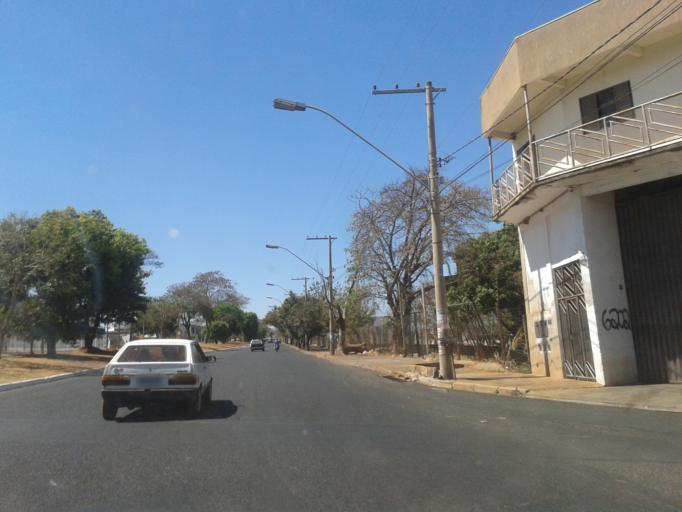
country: BR
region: Minas Gerais
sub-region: Uberlandia
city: Uberlandia
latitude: -18.9335
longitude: -48.2346
